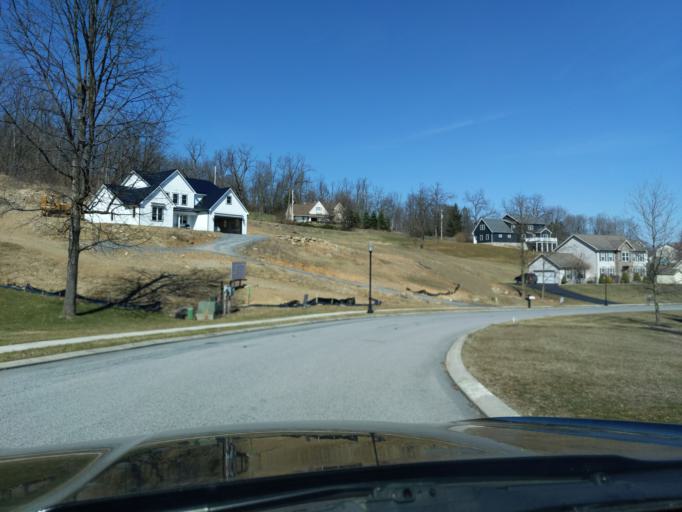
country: US
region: Pennsylvania
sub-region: Blair County
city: Duncansville
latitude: 40.4115
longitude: -78.4236
